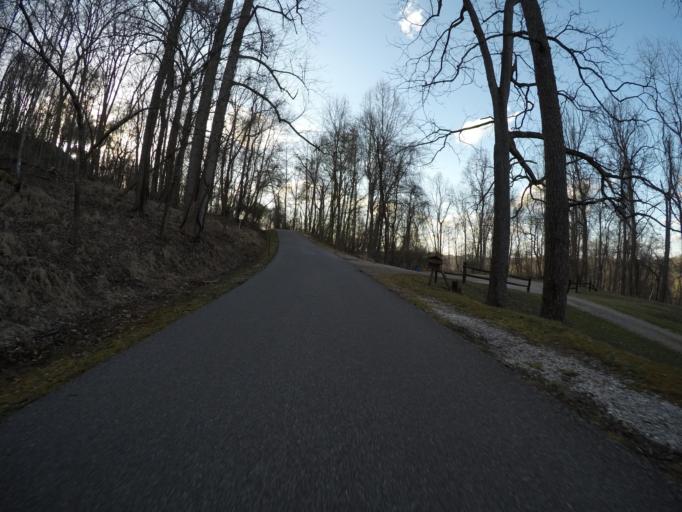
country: US
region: West Virginia
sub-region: Kanawha County
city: Charleston
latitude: 38.3906
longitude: -81.5646
